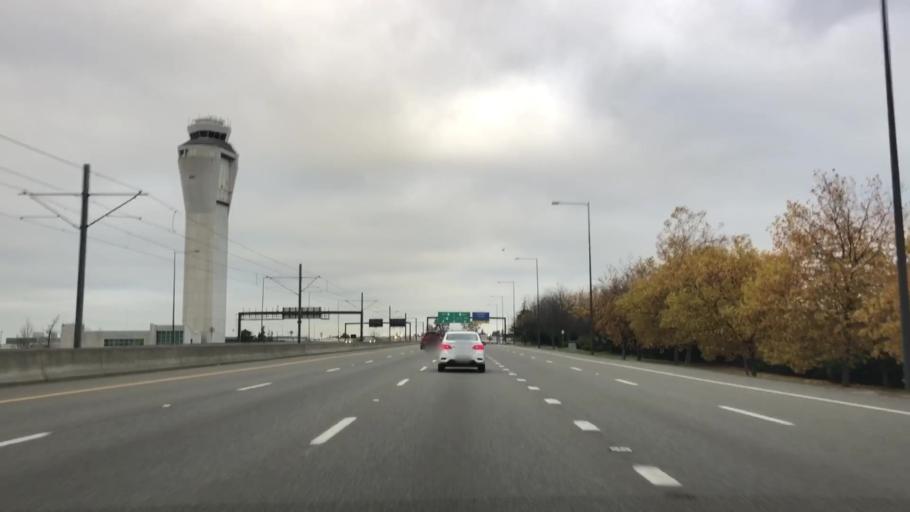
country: US
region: Washington
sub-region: King County
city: SeaTac
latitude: 47.4534
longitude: -122.3003
